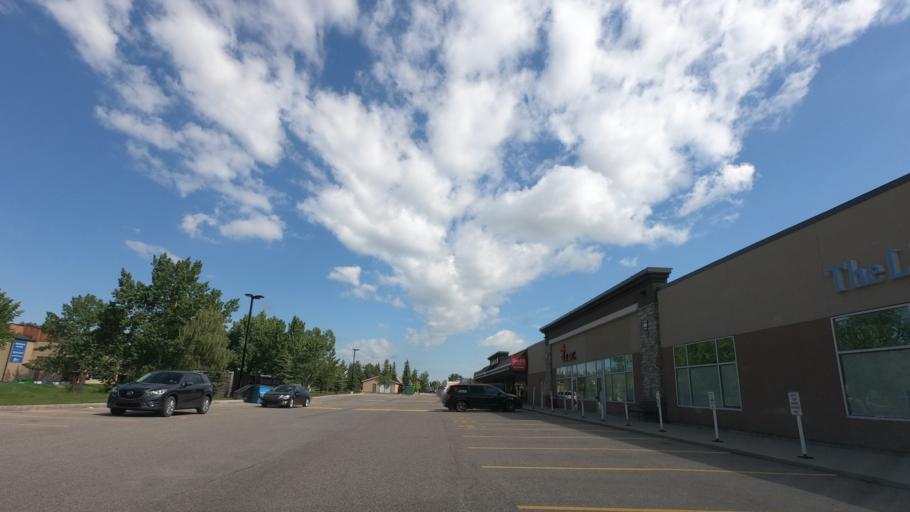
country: CA
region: Alberta
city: Airdrie
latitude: 51.2882
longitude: -114.0160
